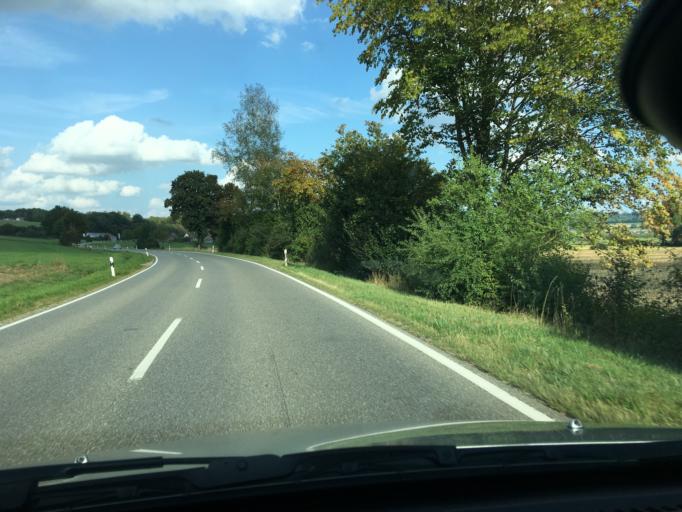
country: DE
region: Baden-Wuerttemberg
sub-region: Tuebingen Region
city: Ingoldingen
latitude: 48.0304
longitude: 9.7611
